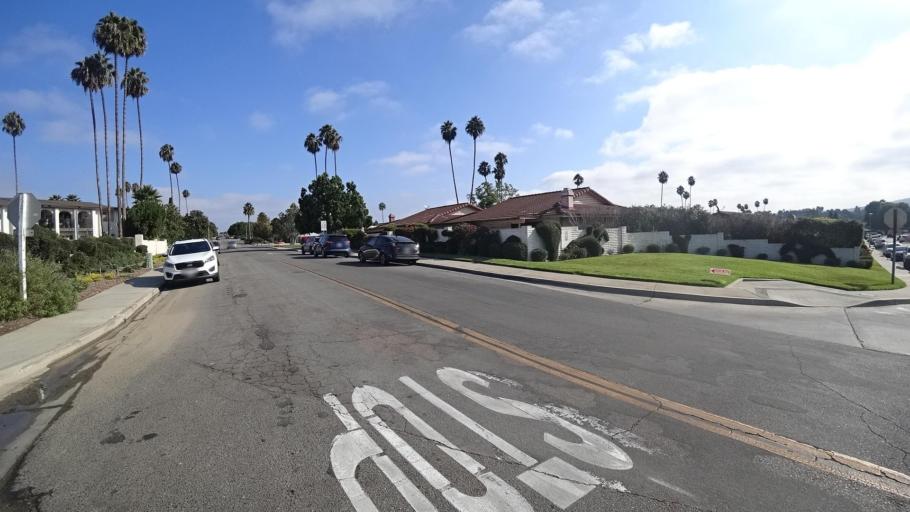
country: US
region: California
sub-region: San Diego County
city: Lake San Marcos
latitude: 33.1254
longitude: -117.2083
